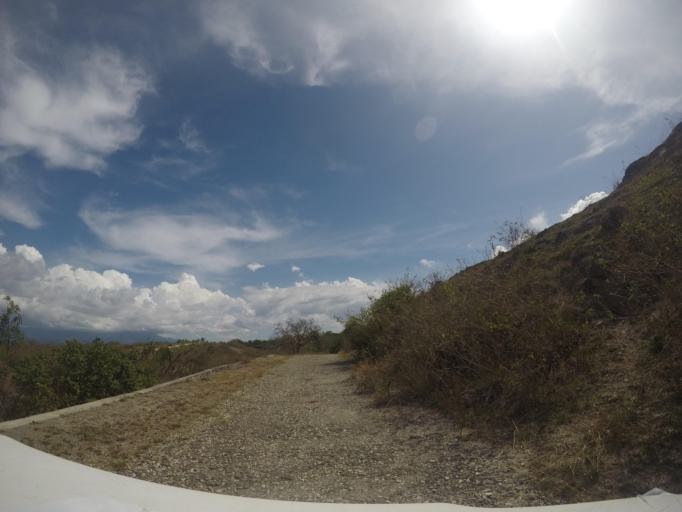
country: TL
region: Baucau
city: Baucau
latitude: -8.4675
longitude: 126.4695
